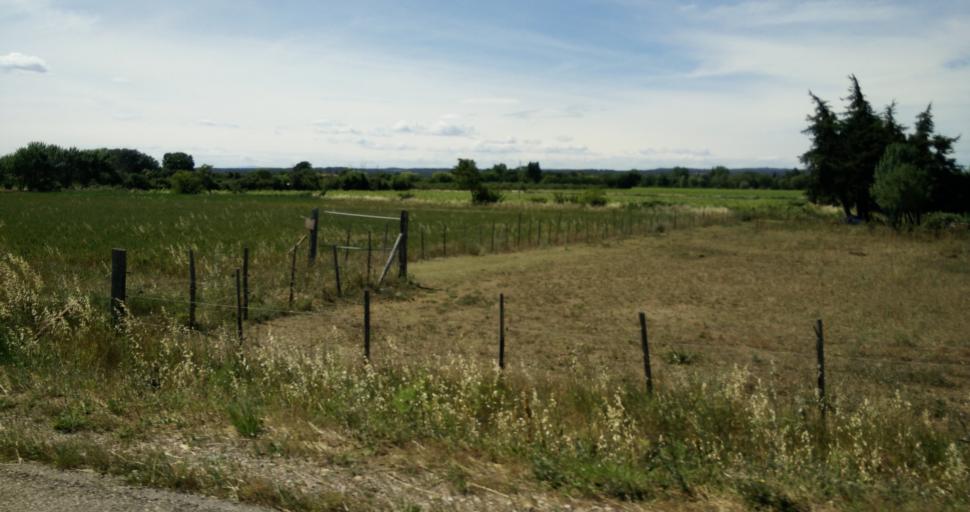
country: FR
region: Languedoc-Roussillon
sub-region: Departement du Gard
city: Aubord
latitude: 43.7436
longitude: 4.2972
